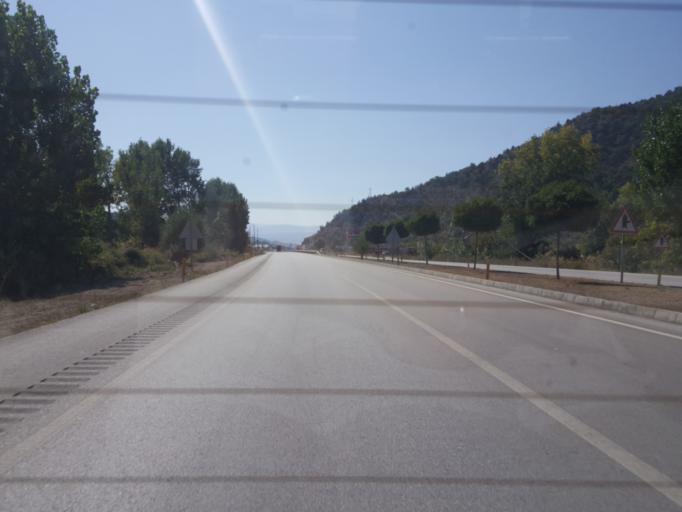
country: TR
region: Corum
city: Osmancik
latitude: 40.9749
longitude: 34.9134
